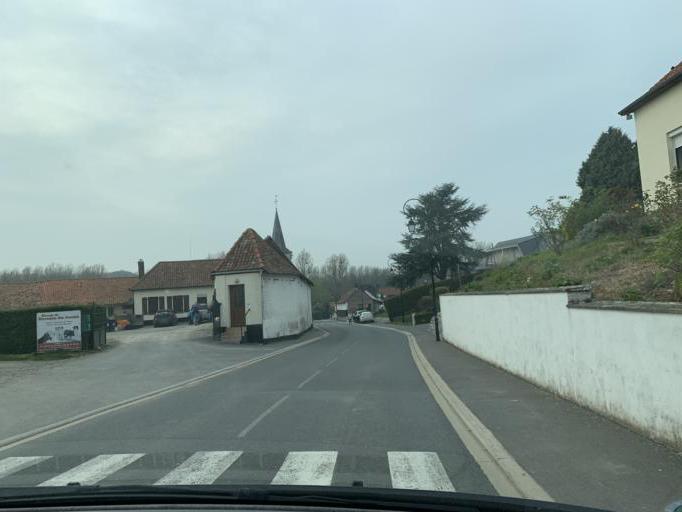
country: FR
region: Nord-Pas-de-Calais
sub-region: Departement du Pas-de-Calais
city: Montreuil
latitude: 50.4984
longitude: 1.7928
